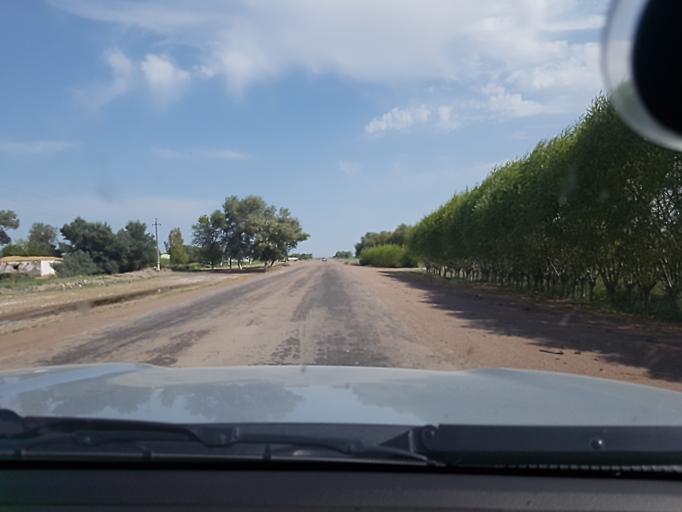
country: TM
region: Dasoguz
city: Boldumsaz
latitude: 42.0912
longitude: 59.7200
